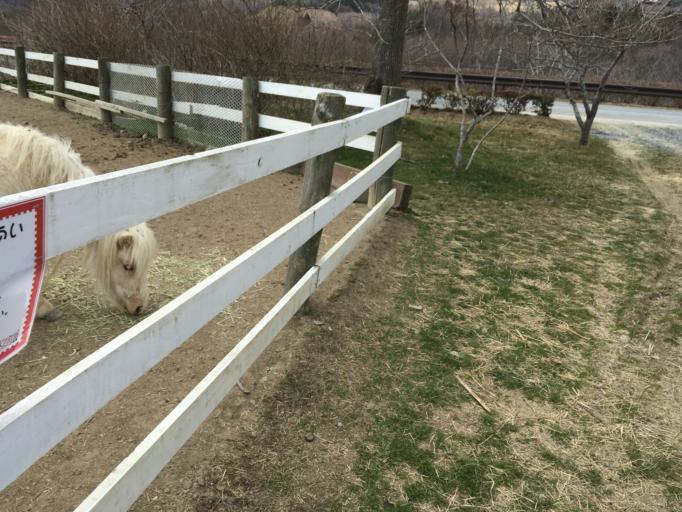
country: JP
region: Iwate
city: Ichinoseki
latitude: 38.8172
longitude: 141.2715
